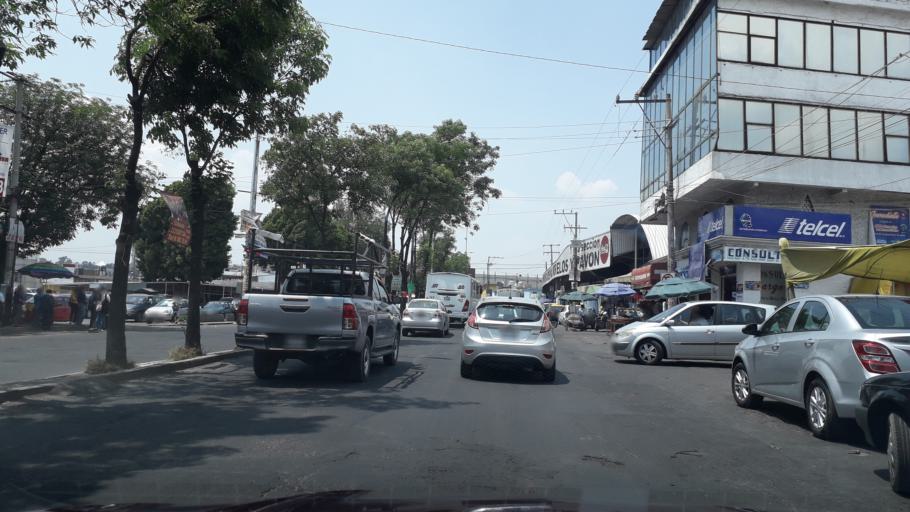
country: MX
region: Puebla
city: Puebla
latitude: 19.0502
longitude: -98.1668
